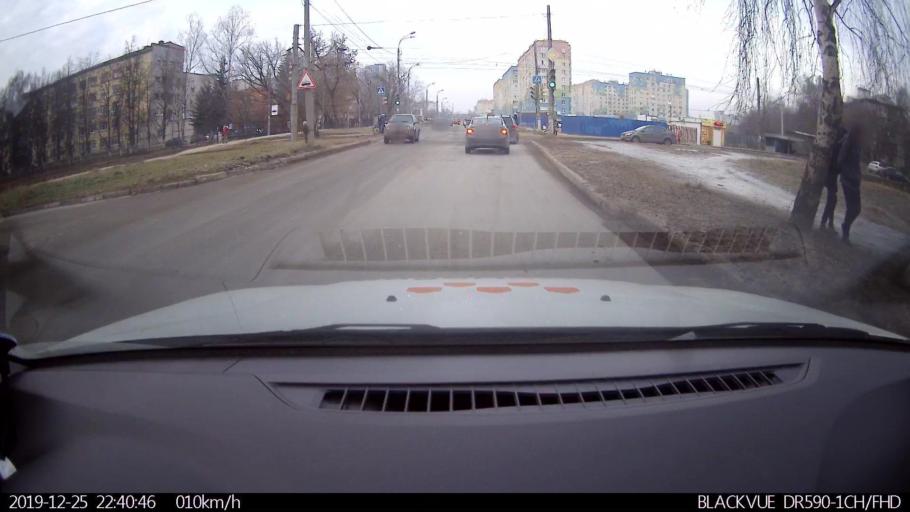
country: RU
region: Nizjnij Novgorod
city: Gorbatovka
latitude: 56.2315
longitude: 43.8472
